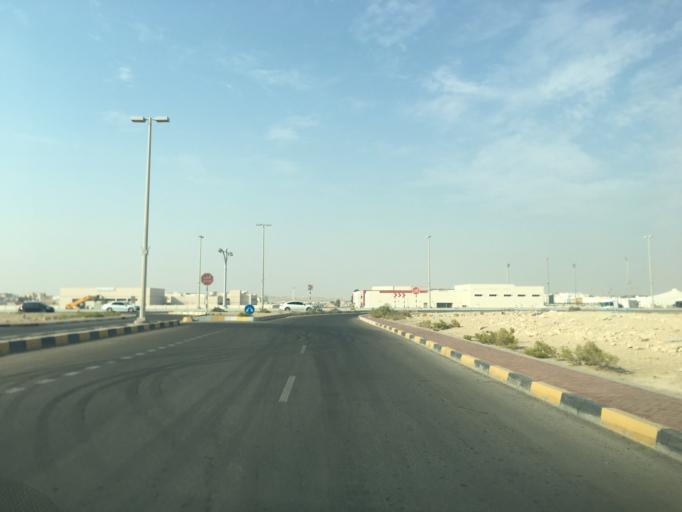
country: AE
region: Abu Dhabi
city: Abu Dhabi
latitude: 24.3032
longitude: 54.6514
